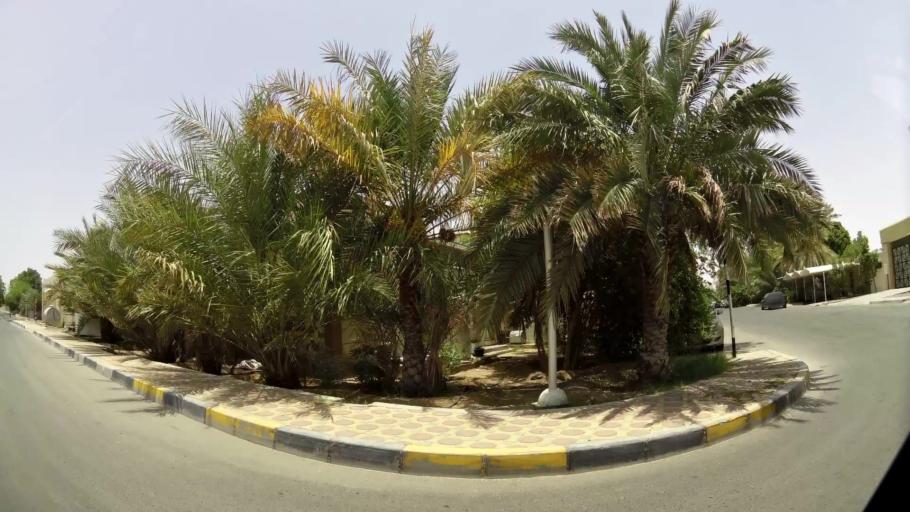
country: AE
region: Abu Dhabi
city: Al Ain
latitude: 24.2144
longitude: 55.7365
